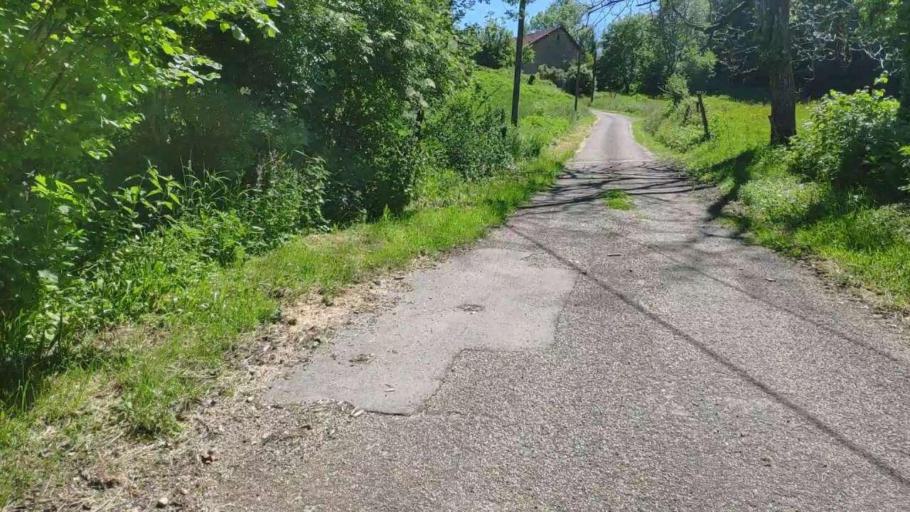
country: FR
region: Franche-Comte
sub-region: Departement du Jura
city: Perrigny
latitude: 46.7314
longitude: 5.6298
